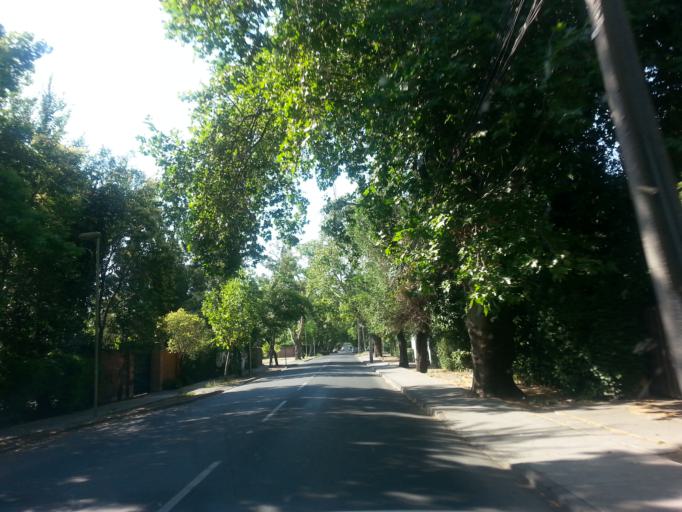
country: CL
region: Santiago Metropolitan
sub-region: Provincia de Santiago
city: Villa Presidente Frei, Nunoa, Santiago, Chile
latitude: -33.3746
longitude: -70.5096
